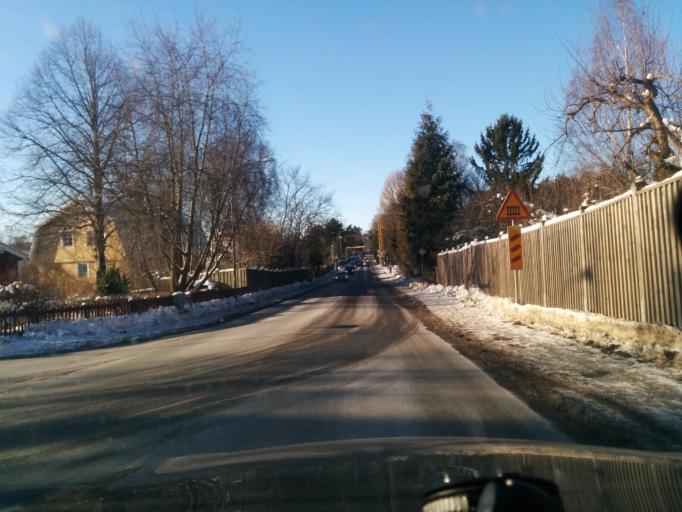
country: SE
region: Stockholm
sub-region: Vallentuna Kommun
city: Vallentuna
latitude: 59.4971
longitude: 18.0737
